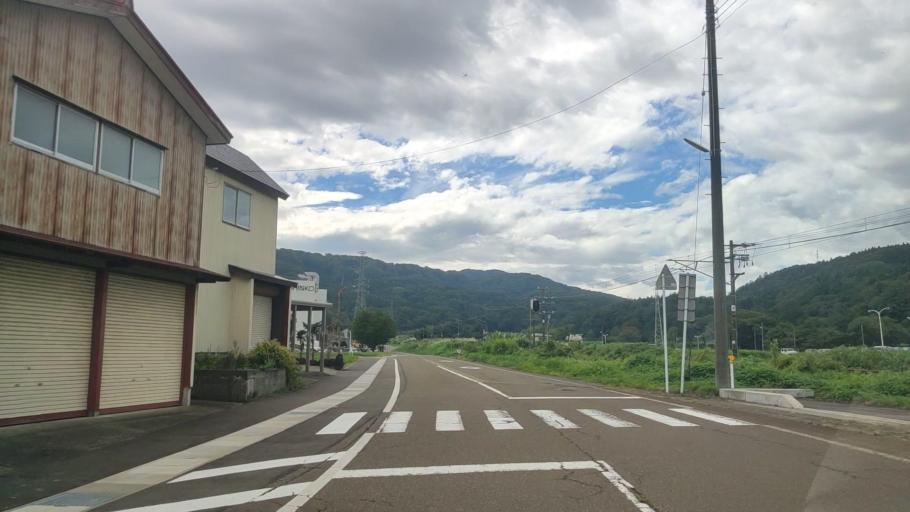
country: JP
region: Niigata
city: Arai
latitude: 37.0067
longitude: 138.2577
